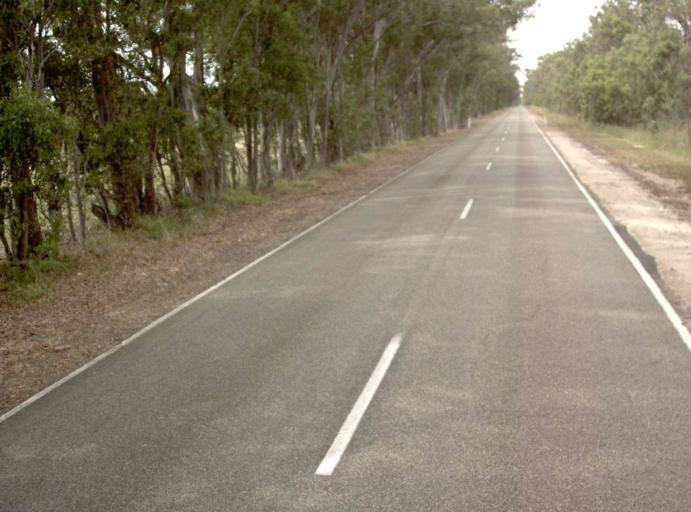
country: AU
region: Victoria
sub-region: Wellington
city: Sale
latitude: -37.8915
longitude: 147.0679
